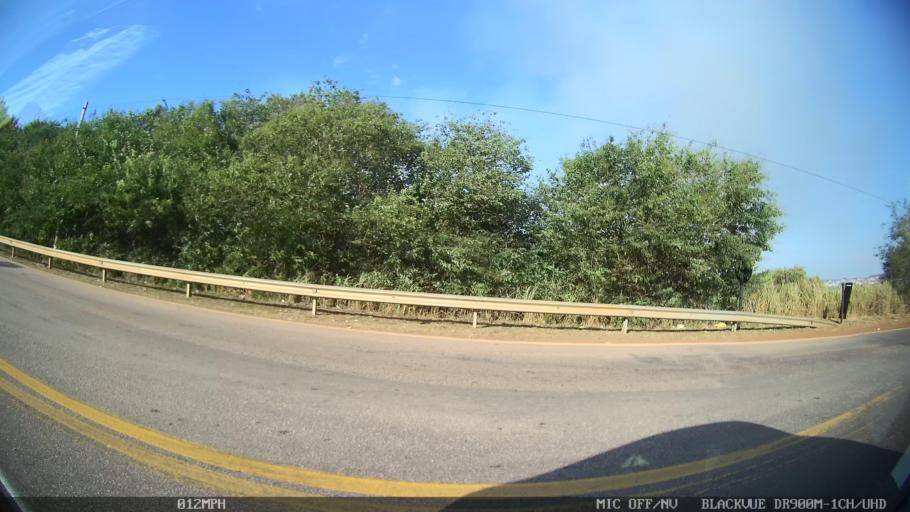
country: BR
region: Sao Paulo
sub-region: Piracicaba
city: Piracicaba
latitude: -22.6936
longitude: -47.5997
